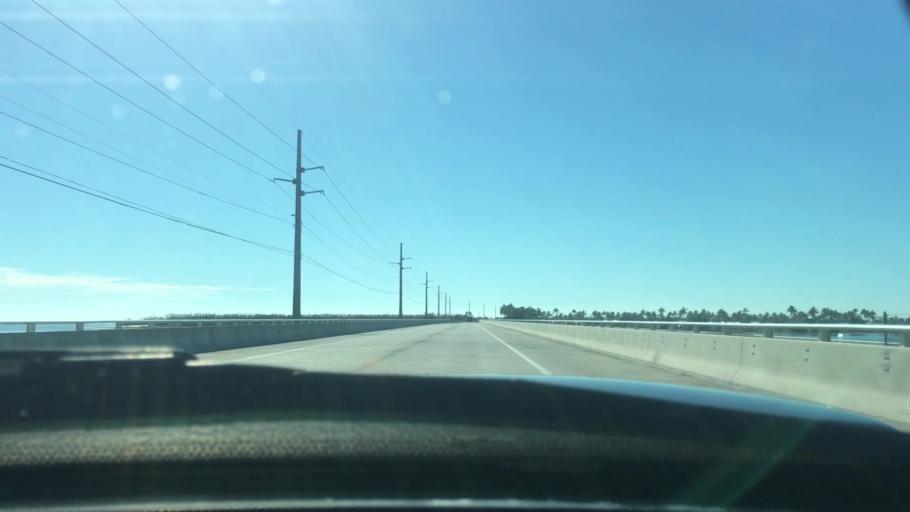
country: US
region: Florida
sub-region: Monroe County
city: Big Pine Key
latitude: 24.6760
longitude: -81.2399
